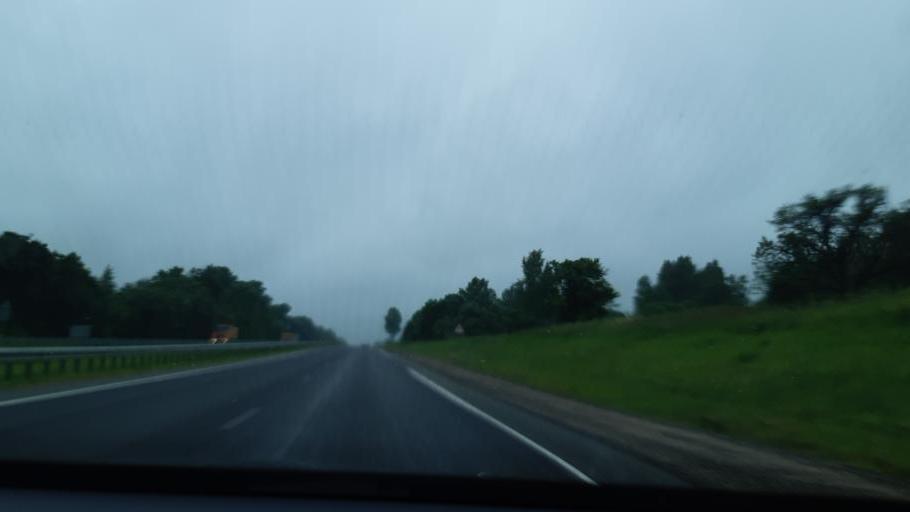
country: RU
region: Smolensk
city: Talashkino
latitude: 54.5691
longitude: 32.2411
